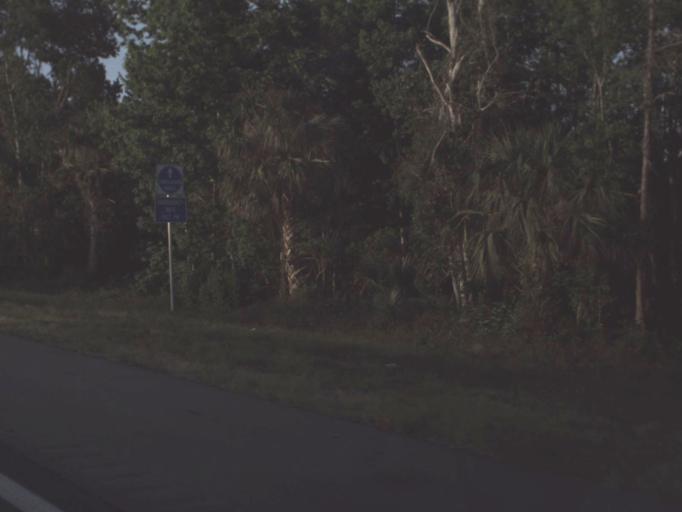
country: US
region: Florida
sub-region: Volusia County
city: Oak Hill
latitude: 28.7911
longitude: -80.8993
